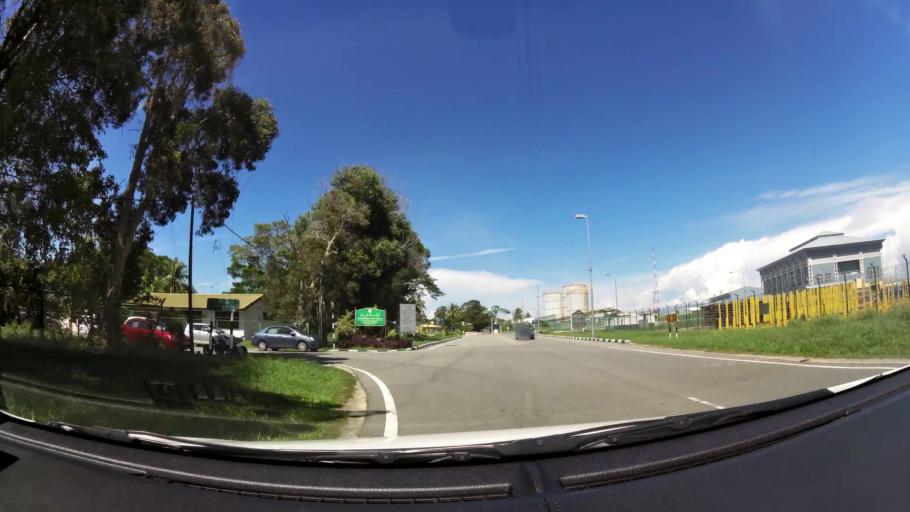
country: BN
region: Brunei and Muara
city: Bandar Seri Begawan
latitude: 5.0344
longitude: 115.0785
